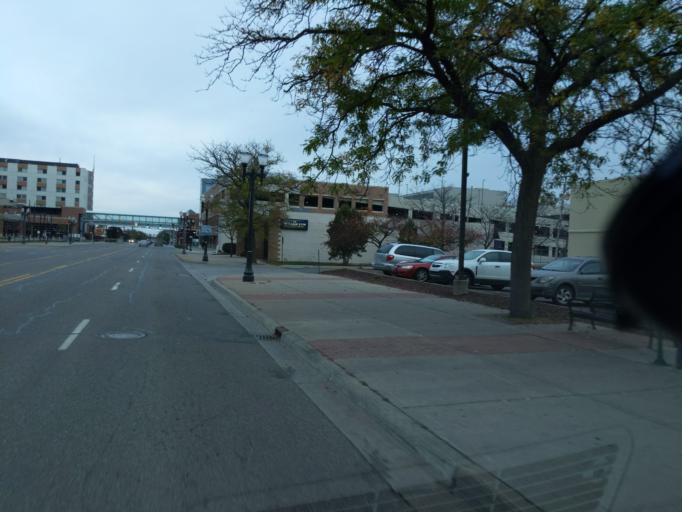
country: US
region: Michigan
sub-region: Ingham County
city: Lansing
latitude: 42.7335
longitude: -84.5373
